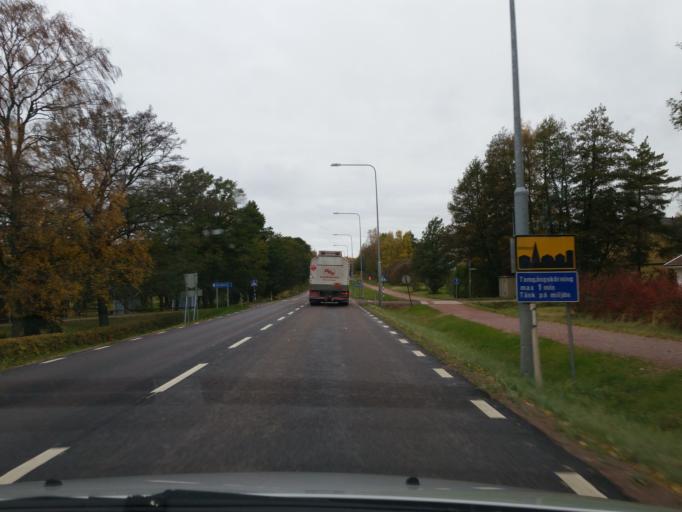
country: AX
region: Mariehamns stad
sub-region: Mariehamn
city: Mariehamn
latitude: 60.1158
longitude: 19.9588
